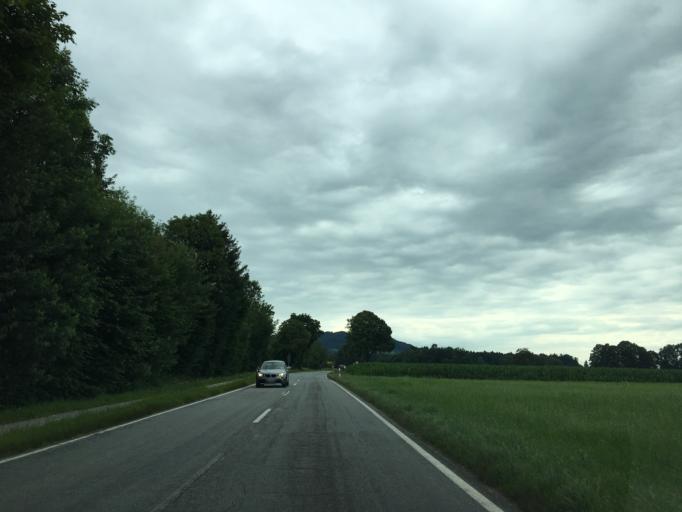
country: DE
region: Bavaria
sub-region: Upper Bavaria
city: Bad Feilnbach
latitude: 47.7655
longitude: 12.0350
